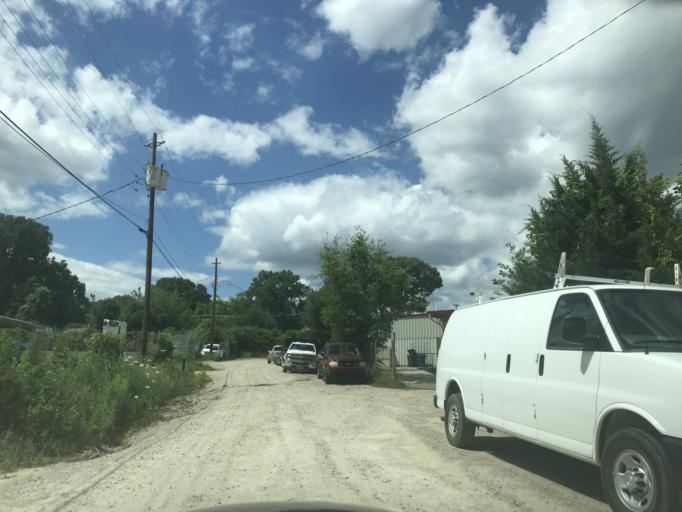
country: US
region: North Carolina
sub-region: Wake County
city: Raleigh
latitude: 35.8037
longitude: -78.6338
